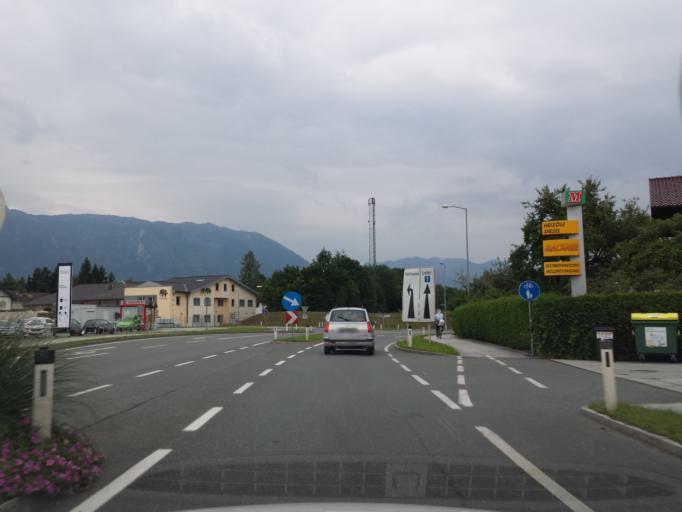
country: DE
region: Bavaria
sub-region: Upper Bavaria
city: Ainring
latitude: 47.7873
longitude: 12.9850
